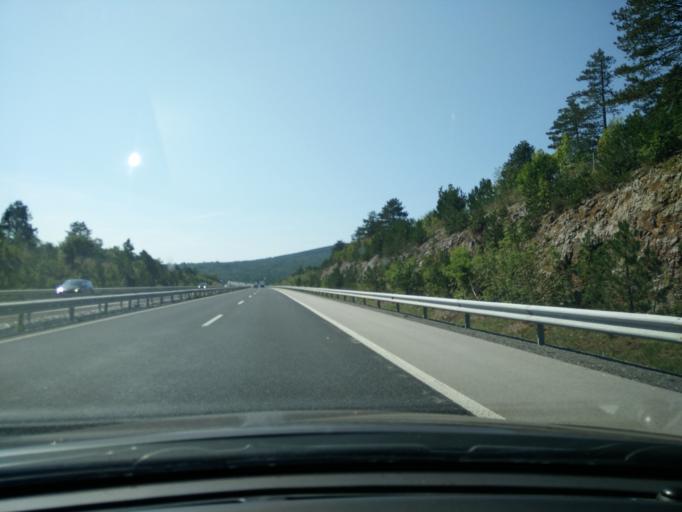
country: SI
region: Divaca
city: Divaca
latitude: 45.6577
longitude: 13.9629
